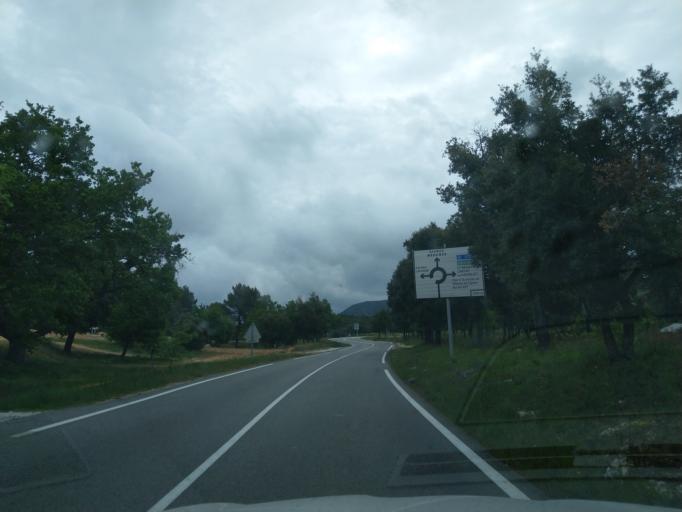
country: FR
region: Provence-Alpes-Cote d'Azur
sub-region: Departement du Var
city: Signes
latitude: 43.2753
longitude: 5.8018
